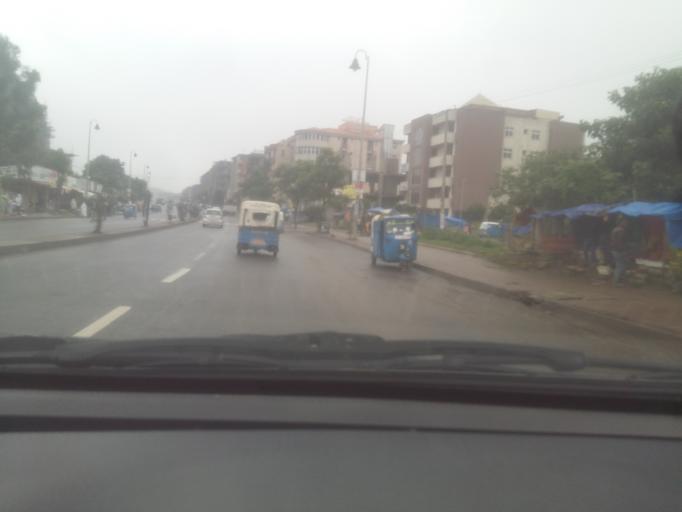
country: ET
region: Adis Abeba
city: Addis Ababa
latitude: 8.9536
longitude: 38.7148
